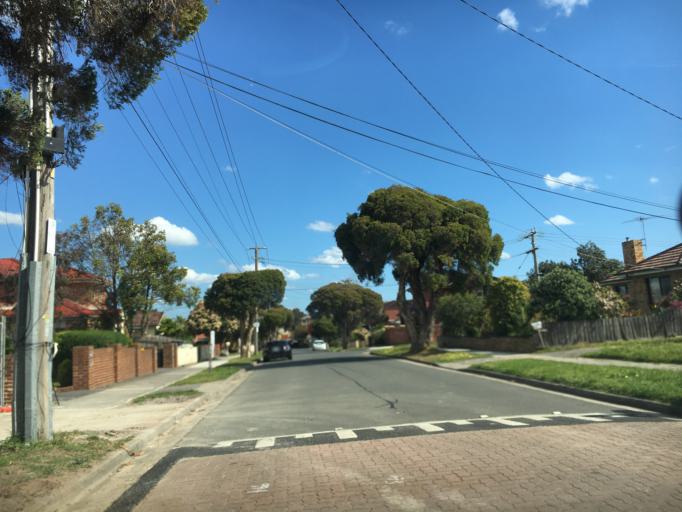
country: AU
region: Victoria
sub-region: Monash
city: Clayton
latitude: -37.9212
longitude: 145.1294
